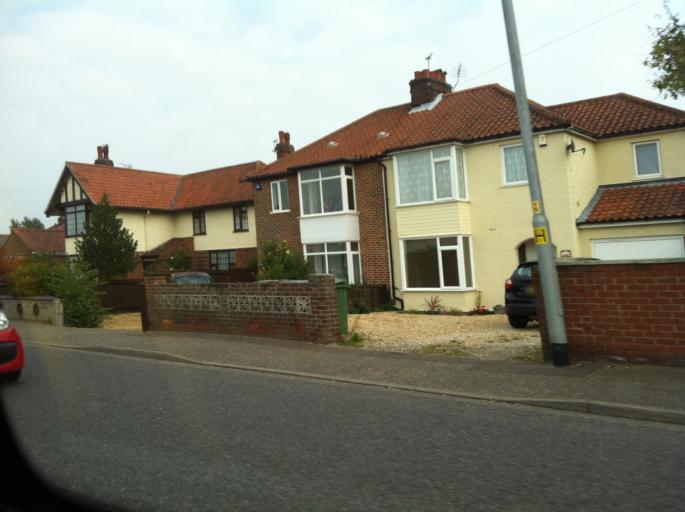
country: GB
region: England
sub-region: Norfolk
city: Norwich
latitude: 52.6591
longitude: 1.2758
